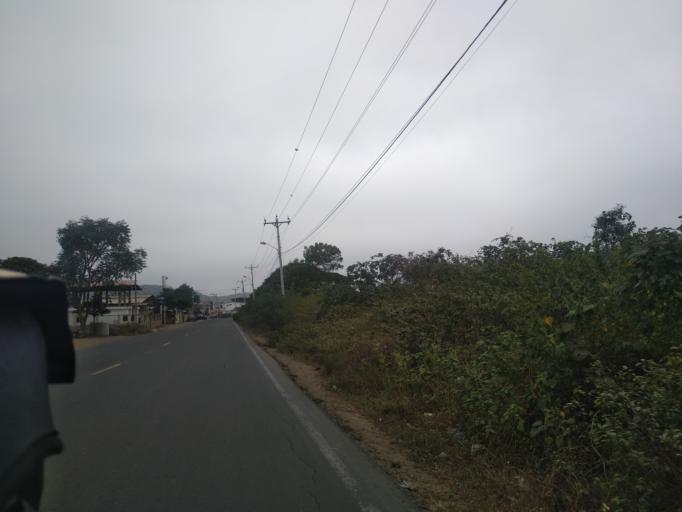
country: EC
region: Manabi
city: Montecristi
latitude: -1.0816
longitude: -80.6773
